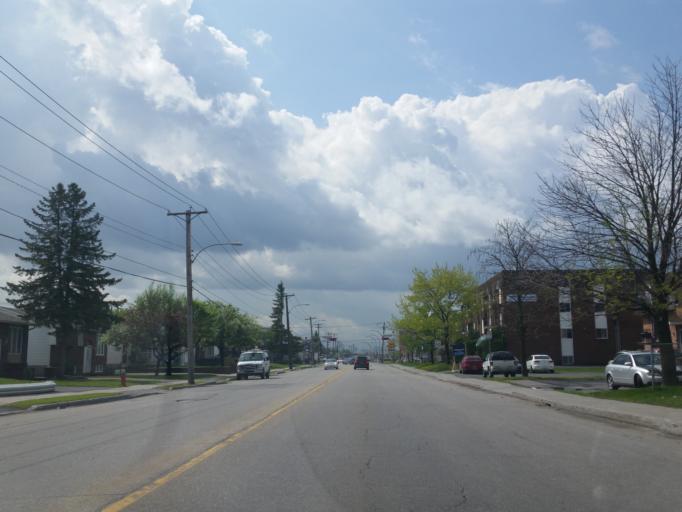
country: CA
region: Quebec
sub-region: Outaouais
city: Gatineau
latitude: 45.4832
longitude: -75.7019
